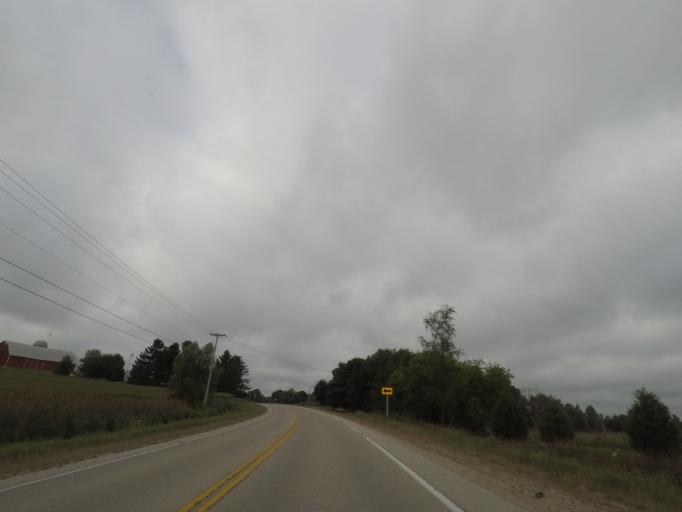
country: US
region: Wisconsin
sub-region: Waukesha County
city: Dousman
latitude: 43.0203
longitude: -88.5587
